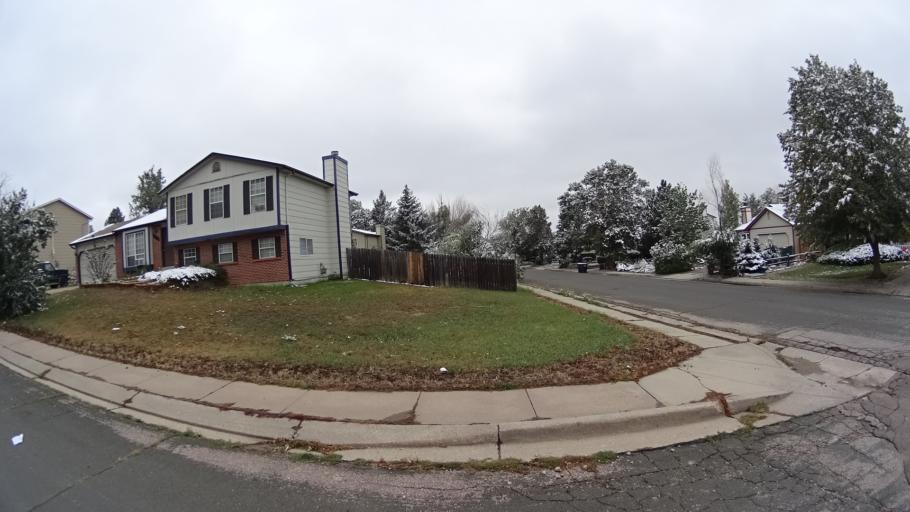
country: US
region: Colorado
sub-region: El Paso County
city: Cimarron Hills
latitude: 38.9290
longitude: -104.7695
